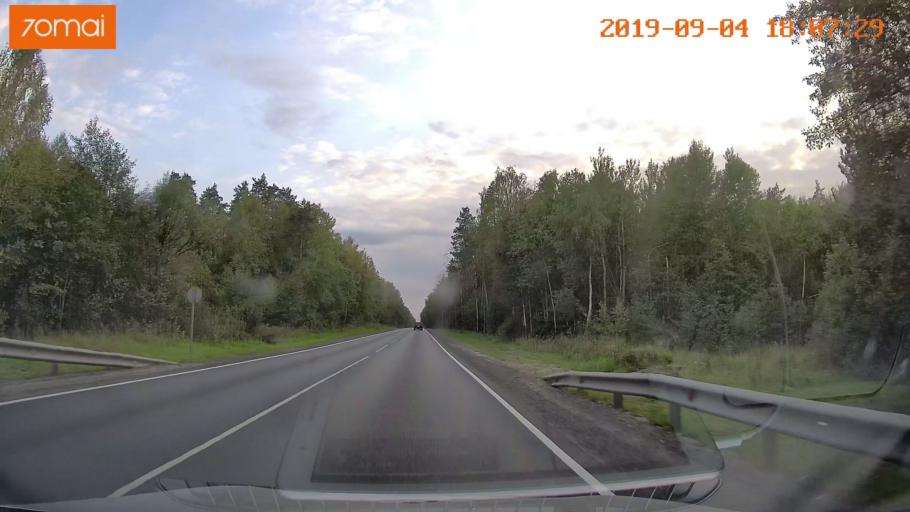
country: RU
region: Moskovskaya
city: Khorlovo
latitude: 55.4183
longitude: 38.8000
